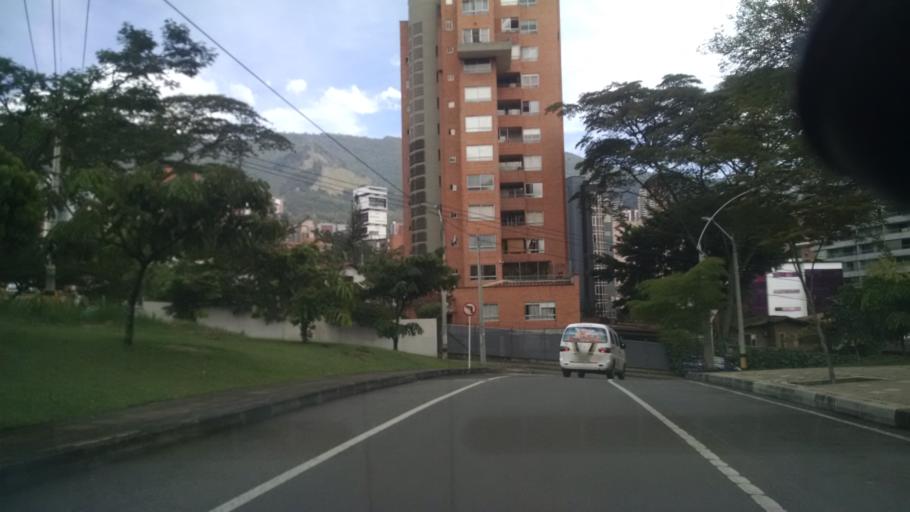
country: CO
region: Antioquia
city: Medellin
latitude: 6.2136
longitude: -75.5645
